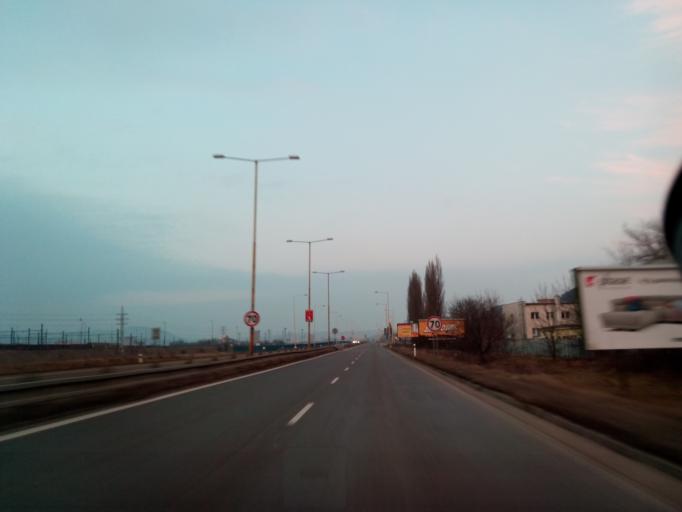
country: SK
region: Kosicky
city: Kosice
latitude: 48.7086
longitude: 21.2792
